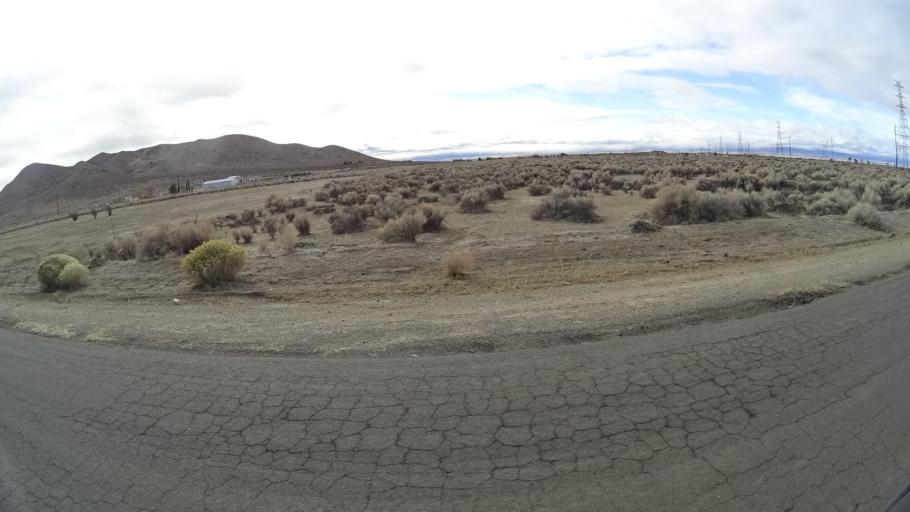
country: US
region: California
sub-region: Kern County
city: Rosamond
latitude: 34.8930
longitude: -118.2928
